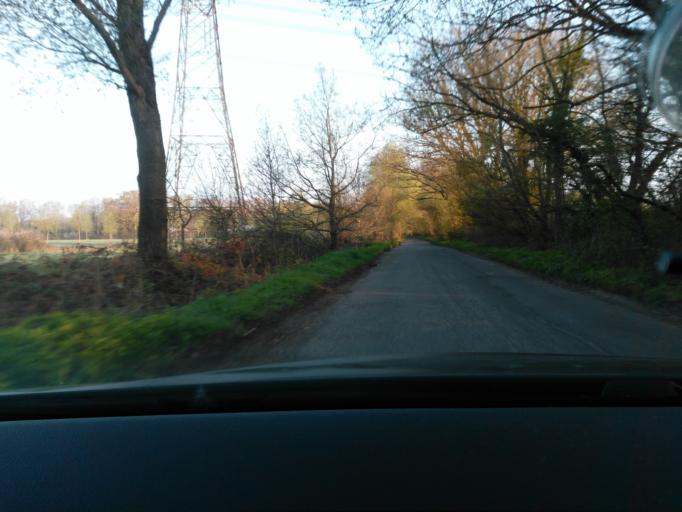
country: GB
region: England
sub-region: West Berkshire
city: Stratfield Mortimer
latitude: 51.3419
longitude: -1.0677
